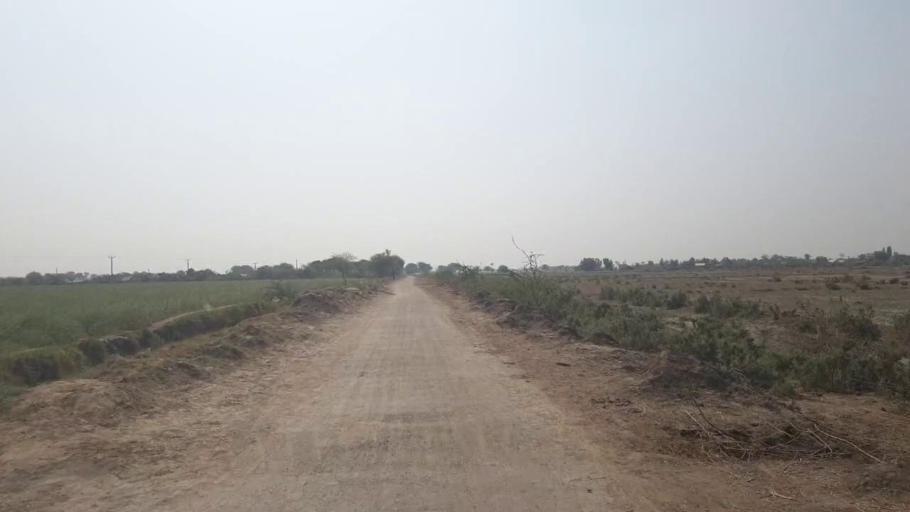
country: PK
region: Sindh
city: Dhoro Naro
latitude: 25.4407
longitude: 69.6261
